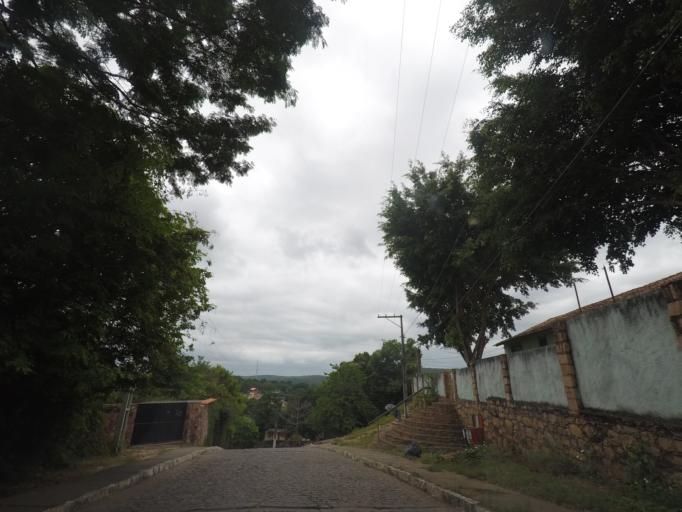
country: BR
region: Bahia
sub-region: Andarai
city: Vera Cruz
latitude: -12.5647
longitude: -41.3924
